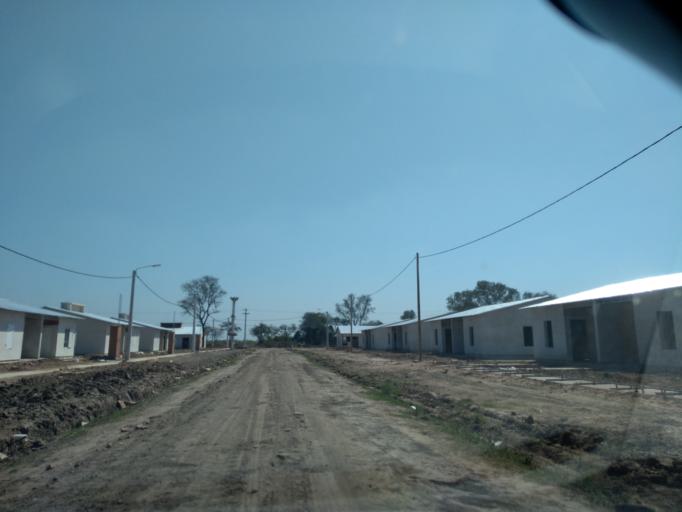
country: AR
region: Chaco
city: Resistencia
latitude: -27.4130
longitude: -58.9564
